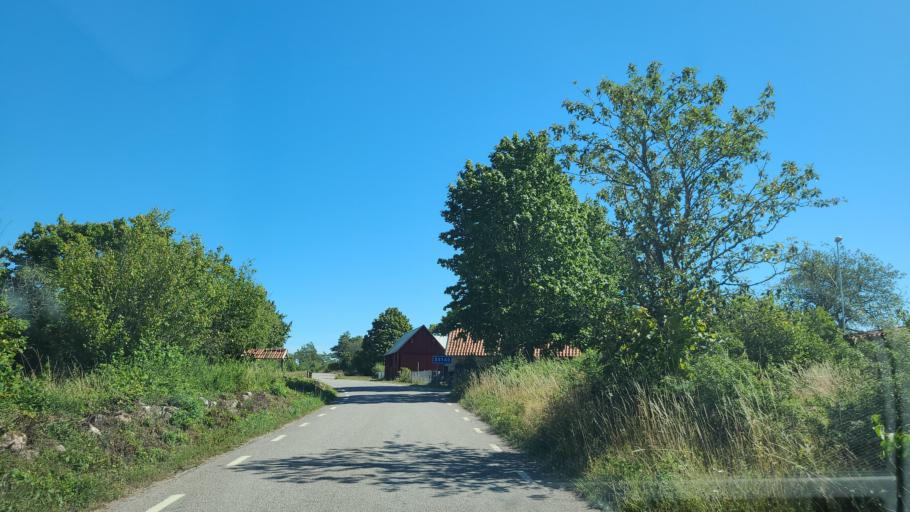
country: SE
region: Kalmar
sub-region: Borgholms Kommun
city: Borgholm
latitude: 56.7450
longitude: 16.6796
